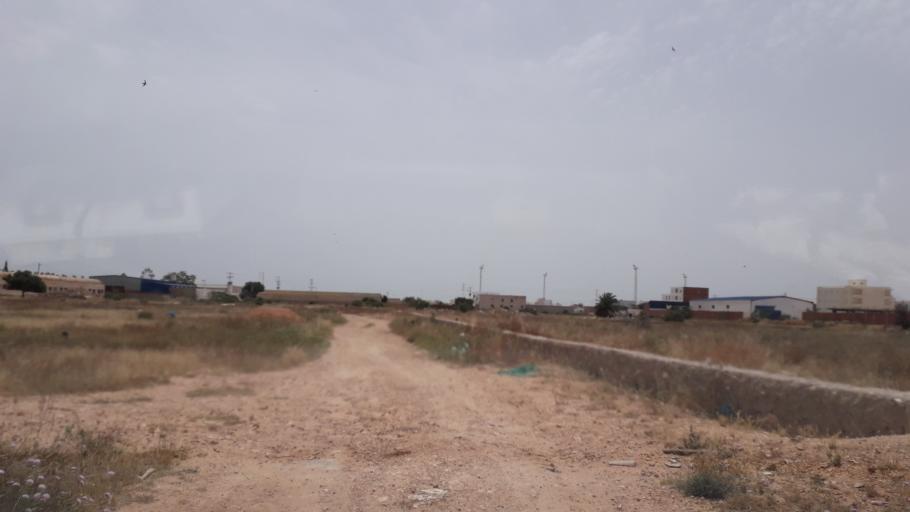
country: TN
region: Safaqis
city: Al Qarmadah
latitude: 34.8472
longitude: 10.7569
